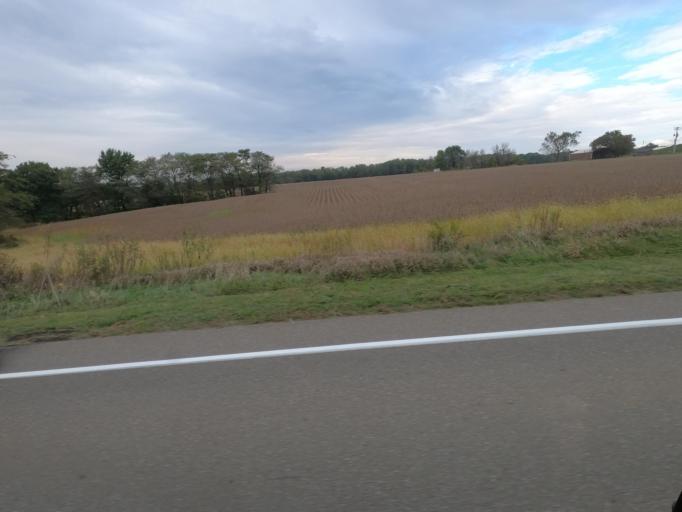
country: US
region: Iowa
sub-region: Henry County
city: Mount Pleasant
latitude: 40.7845
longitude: -91.6805
